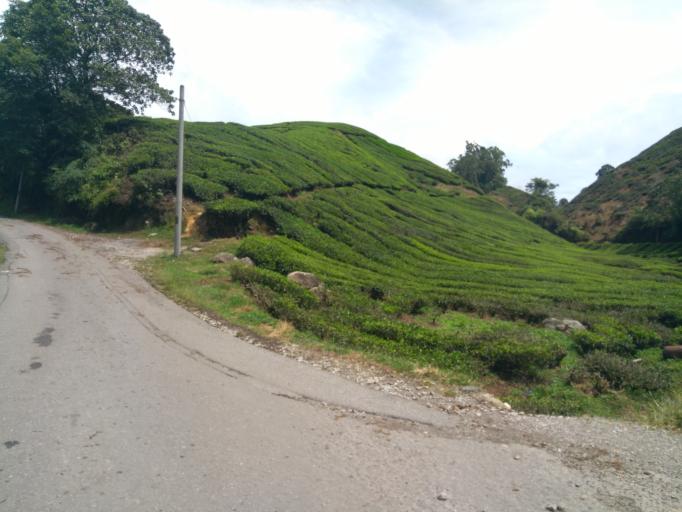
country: MY
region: Pahang
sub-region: Cameron Highlands
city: Tanah Rata
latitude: 4.5208
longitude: 101.4043
